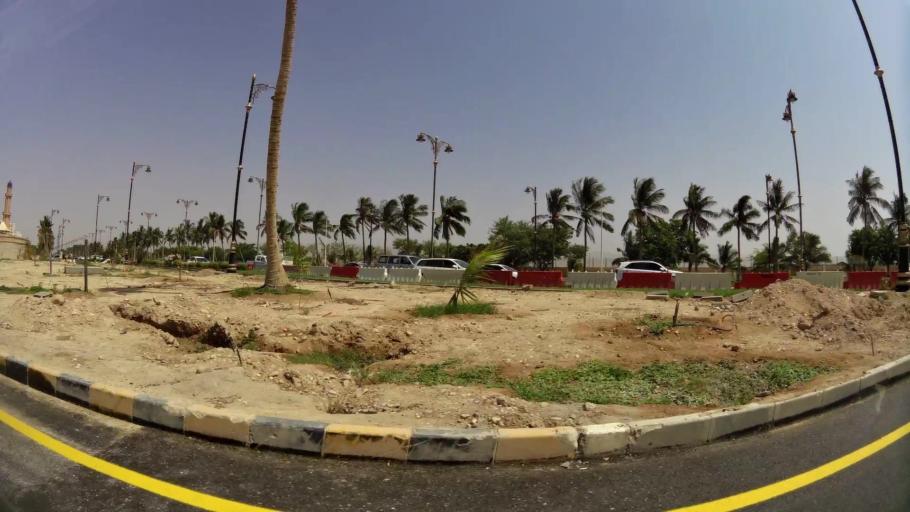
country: OM
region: Zufar
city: Salalah
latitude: 17.0230
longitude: 54.1021
